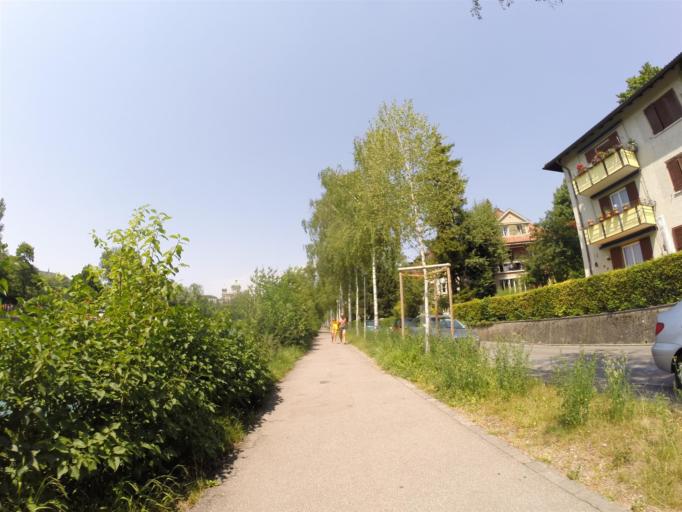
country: CH
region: Bern
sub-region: Bern-Mittelland District
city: Bern
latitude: 46.9406
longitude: 7.4452
